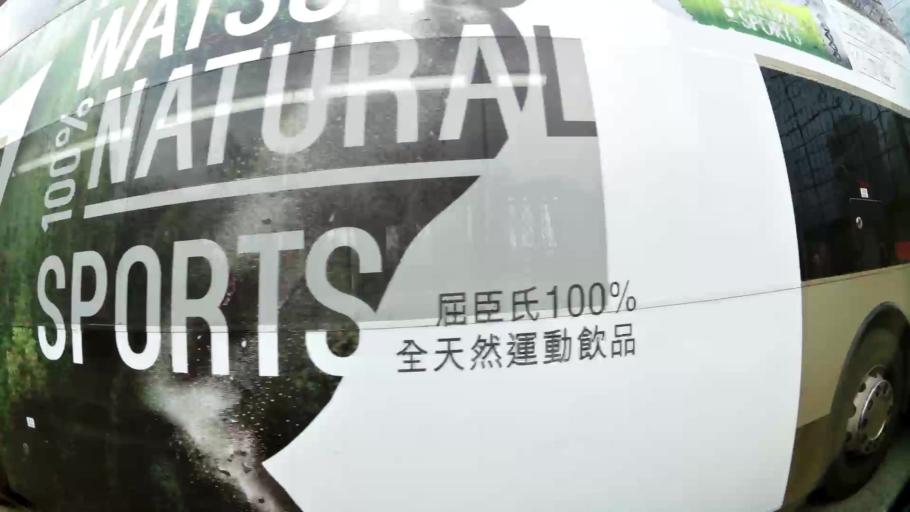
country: HK
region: Kowloon City
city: Kowloon
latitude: 22.3271
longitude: 114.2058
